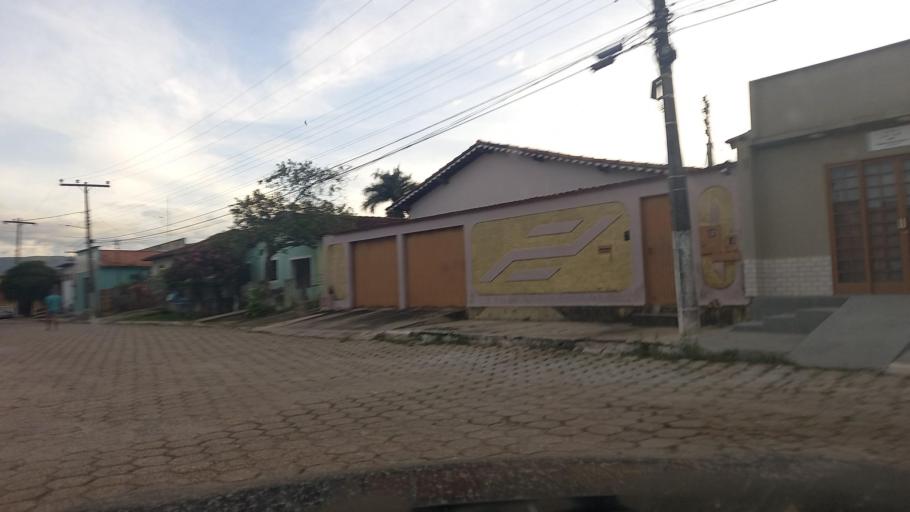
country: BR
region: Goias
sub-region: Cavalcante
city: Cavalcante
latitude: -13.7967
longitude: -47.4605
